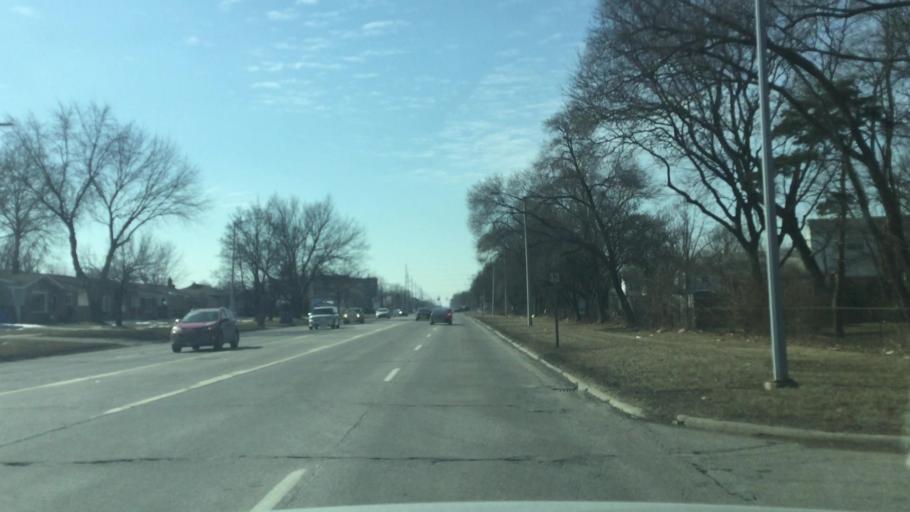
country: US
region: Michigan
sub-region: Wayne County
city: Garden City
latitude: 42.3114
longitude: -83.3260
